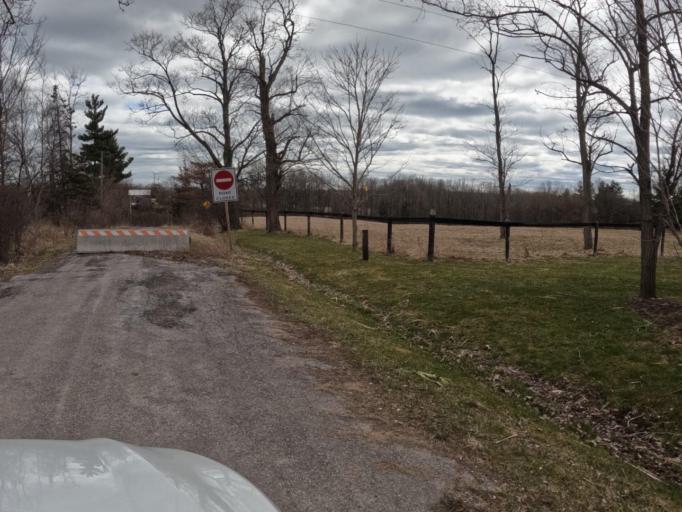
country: CA
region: Ontario
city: Norfolk County
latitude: 42.8264
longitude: -80.1694
